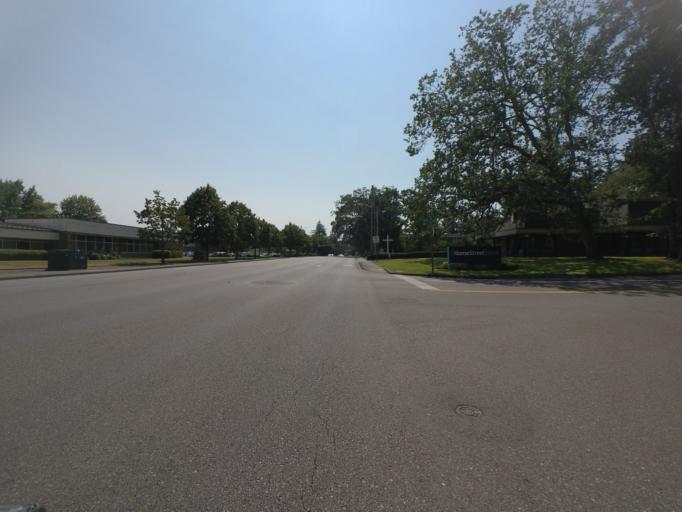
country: US
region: Washington
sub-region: Pierce County
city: Lakewood
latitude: 47.1596
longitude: -122.5207
